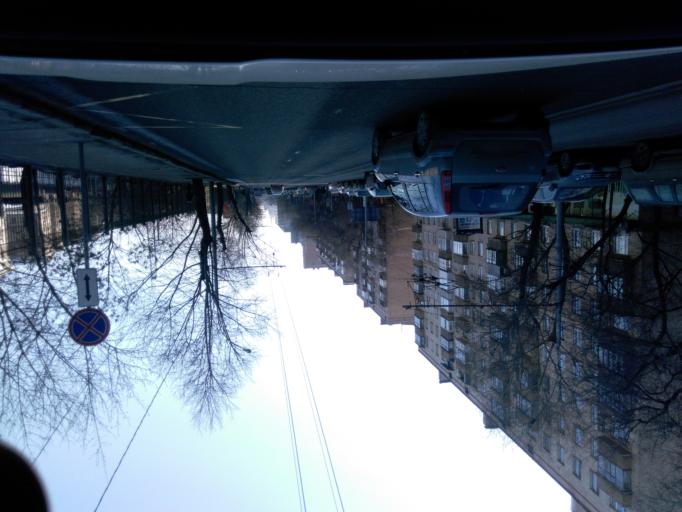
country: RU
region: Moscow
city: Mar'ina Roshcha
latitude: 55.7846
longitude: 37.5870
